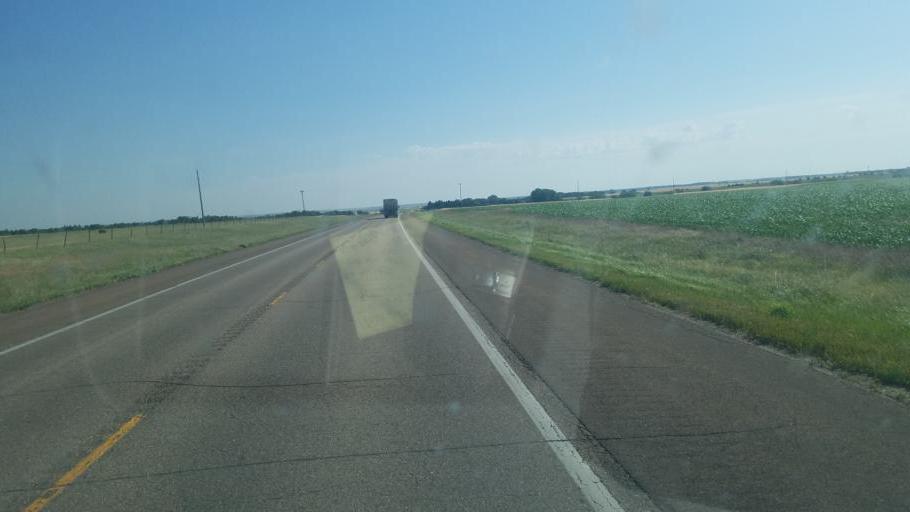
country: US
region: Kansas
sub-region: Barton County
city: Great Bend
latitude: 38.3965
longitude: -98.6725
